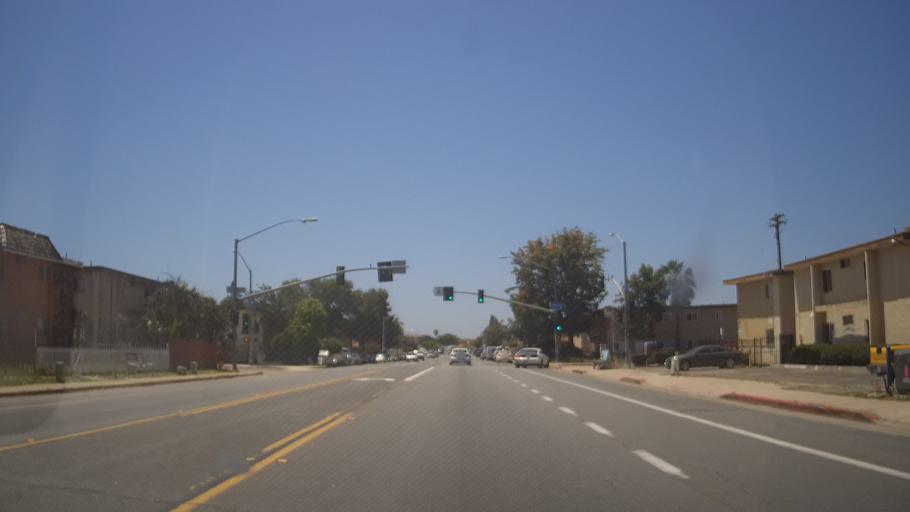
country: US
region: California
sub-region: San Diego County
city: National City
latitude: 32.7073
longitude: -117.0782
